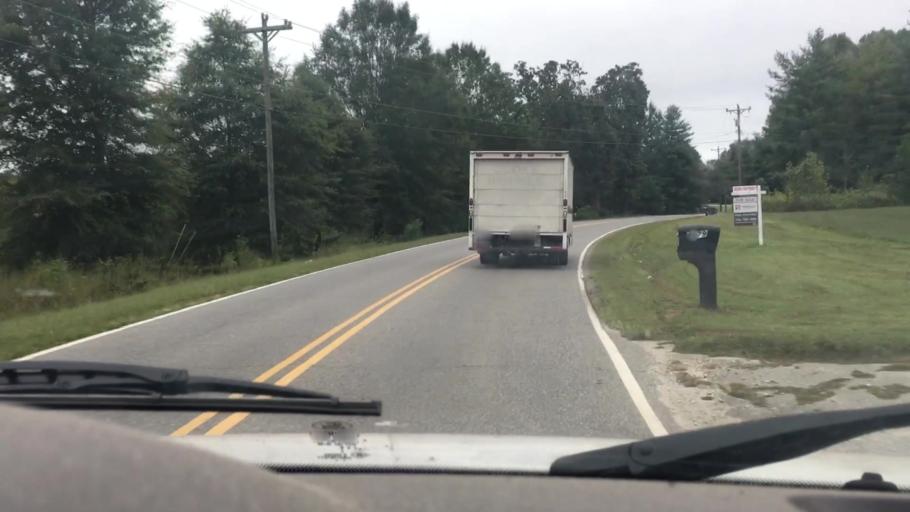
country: US
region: North Carolina
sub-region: Catawba County
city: Lake Norman of Catawba
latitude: 35.5791
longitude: -80.9887
